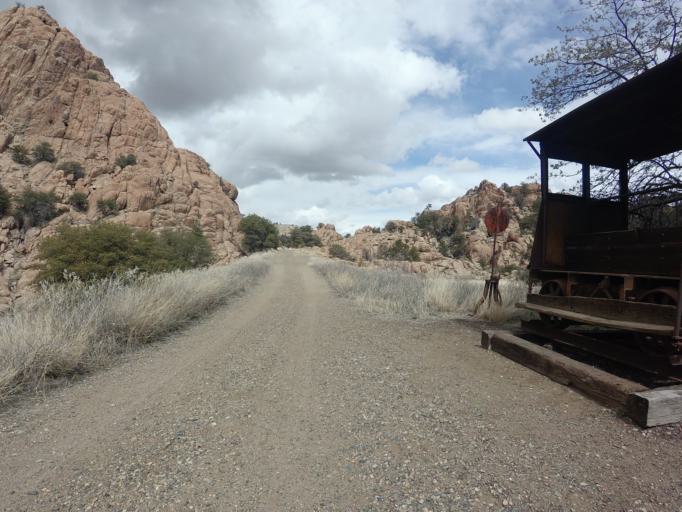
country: US
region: Arizona
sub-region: Yavapai County
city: Prescott Valley
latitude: 34.6062
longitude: -112.3905
